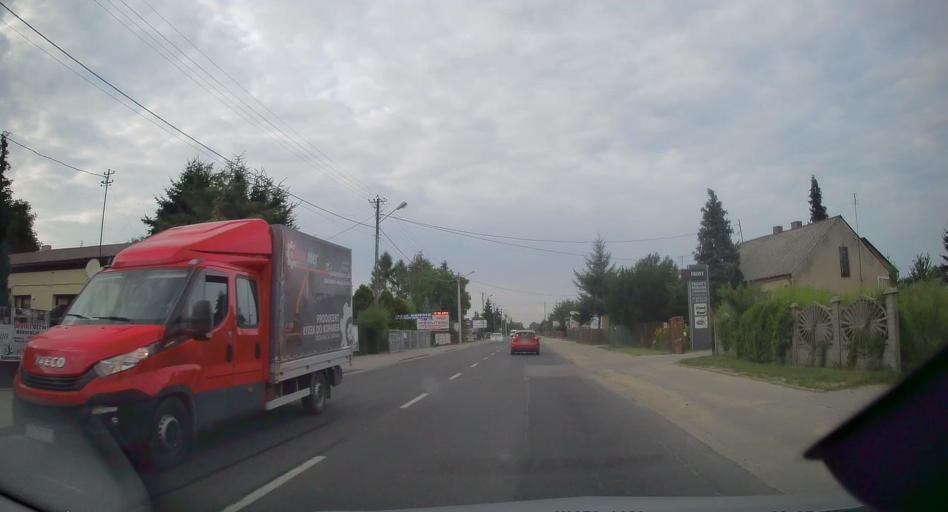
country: PL
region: Lodz Voivodeship
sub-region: Powiat radomszczanski
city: Radomsko
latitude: 51.0859
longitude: 19.4540
